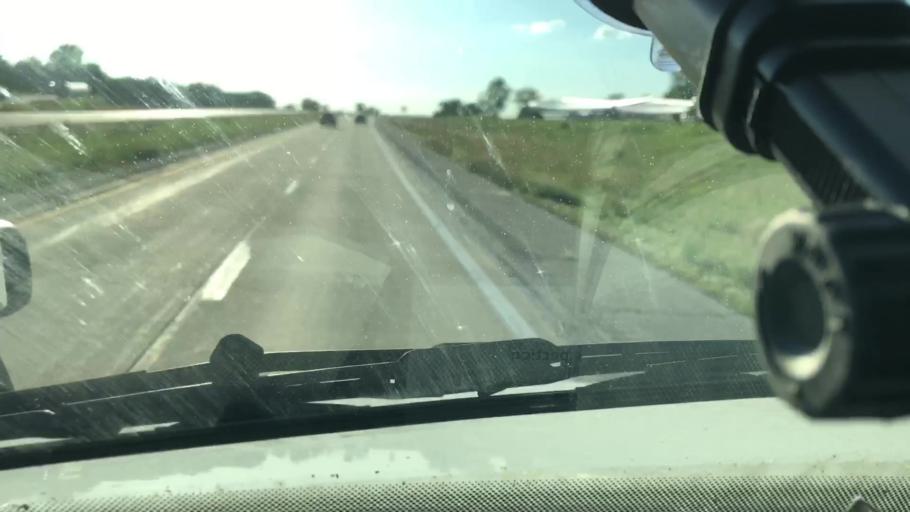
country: US
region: Iowa
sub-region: Pottawattamie County
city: Avoca
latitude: 41.4990
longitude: -95.4910
